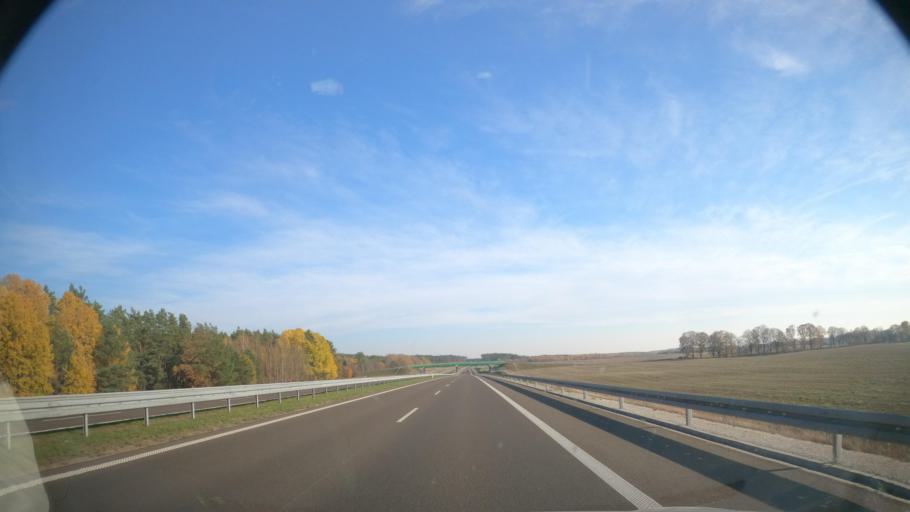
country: PL
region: West Pomeranian Voivodeship
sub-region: Powiat walecki
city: Walcz
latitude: 53.2947
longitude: 16.4825
